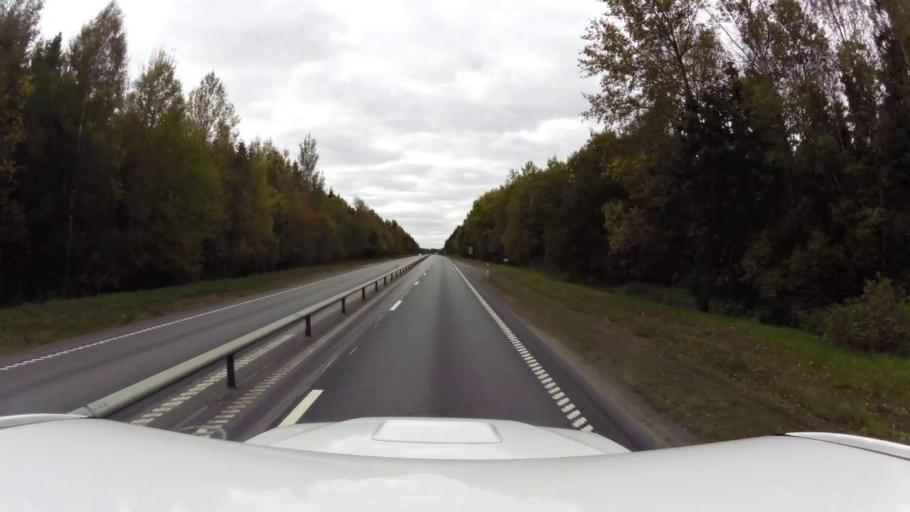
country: SE
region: OEstergoetland
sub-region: Linkopings Kommun
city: Malmslatt
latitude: 58.3796
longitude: 15.5424
